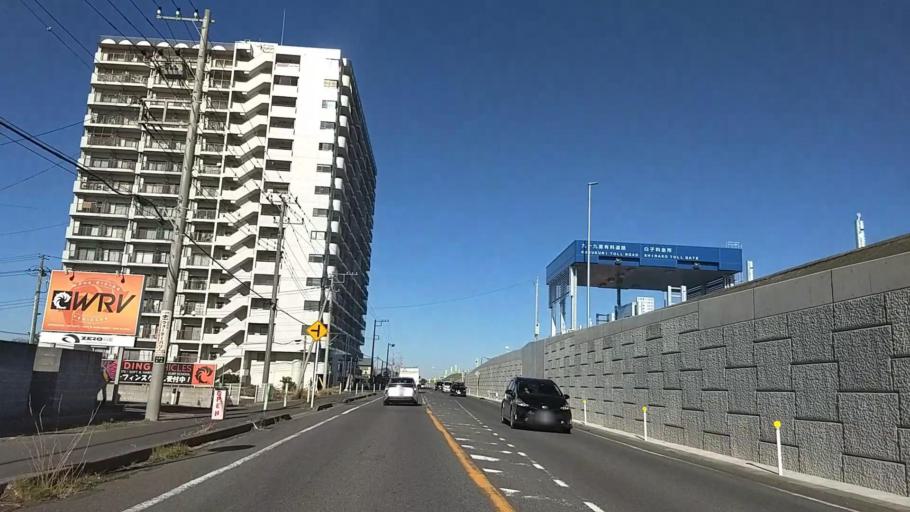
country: JP
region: Chiba
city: Togane
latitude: 35.4524
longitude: 140.4036
